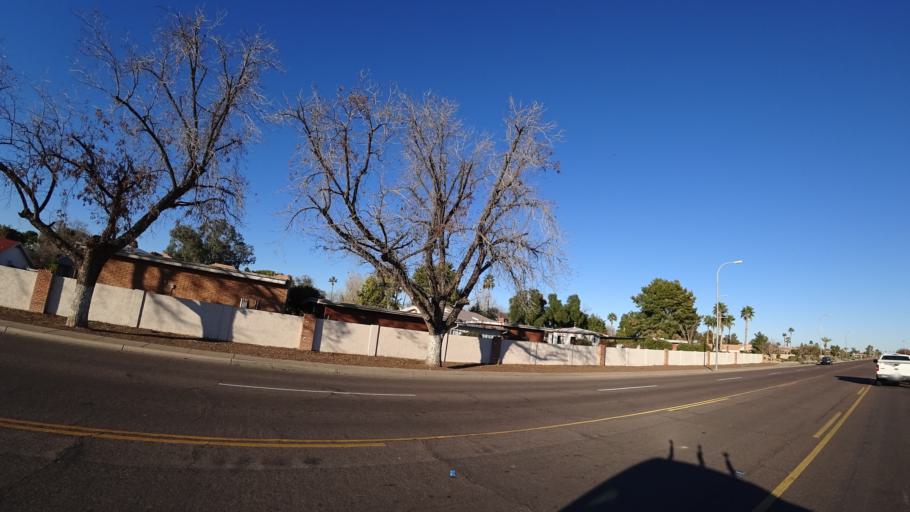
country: US
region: Arizona
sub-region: Maricopa County
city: Tolleson
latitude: 33.4506
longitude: -112.2519
